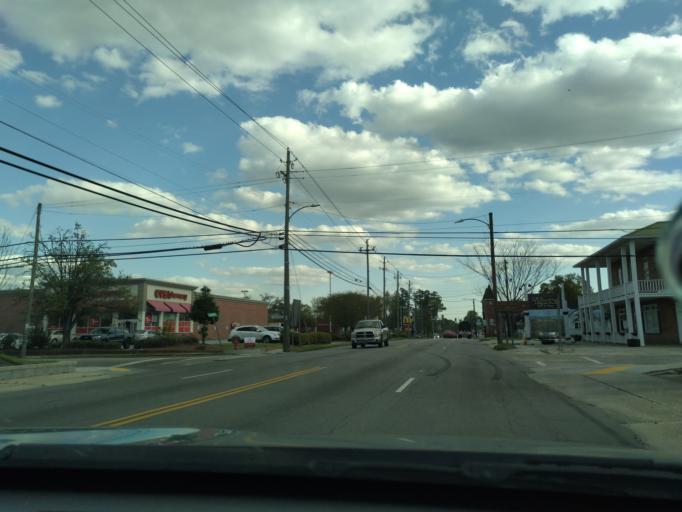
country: US
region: South Carolina
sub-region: Williamsburg County
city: Kingstree
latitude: 33.6647
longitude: -79.8339
